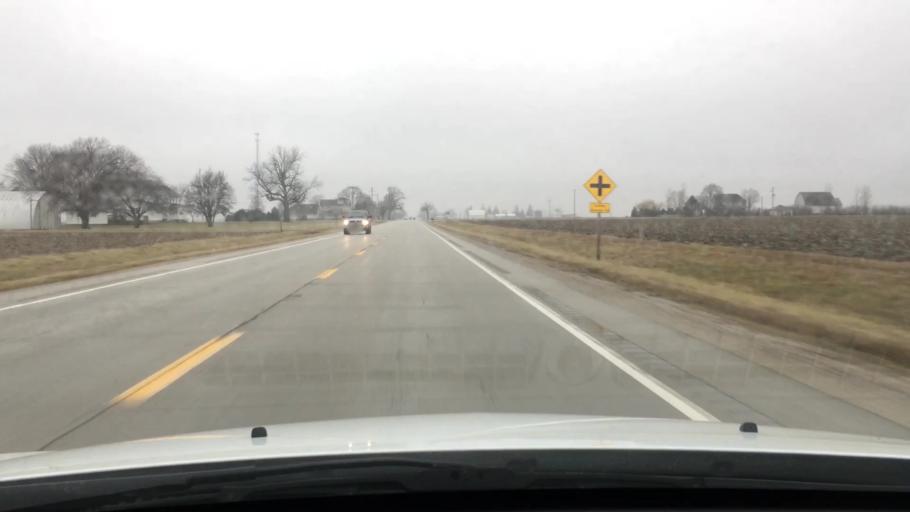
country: US
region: Illinois
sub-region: Livingston County
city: Flanagan
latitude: 40.8711
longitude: -88.8695
